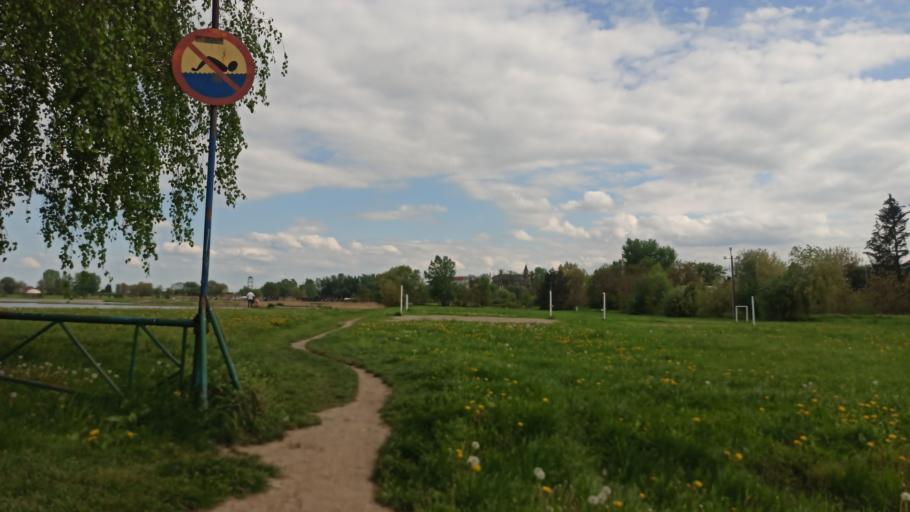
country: PL
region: Subcarpathian Voivodeship
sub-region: Powiat jaroslawski
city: Radymno
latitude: 49.9533
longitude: 22.8235
